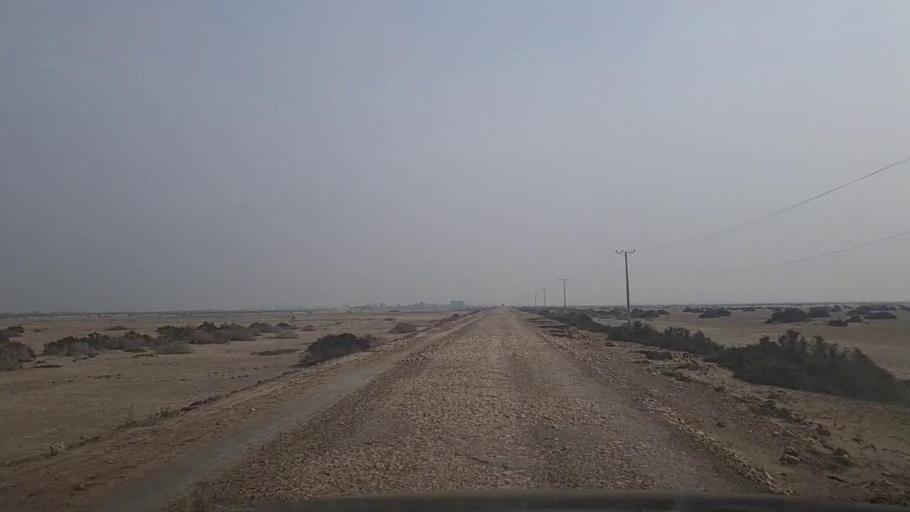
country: PK
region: Sindh
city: Mirpur Sakro
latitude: 24.4658
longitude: 67.6843
